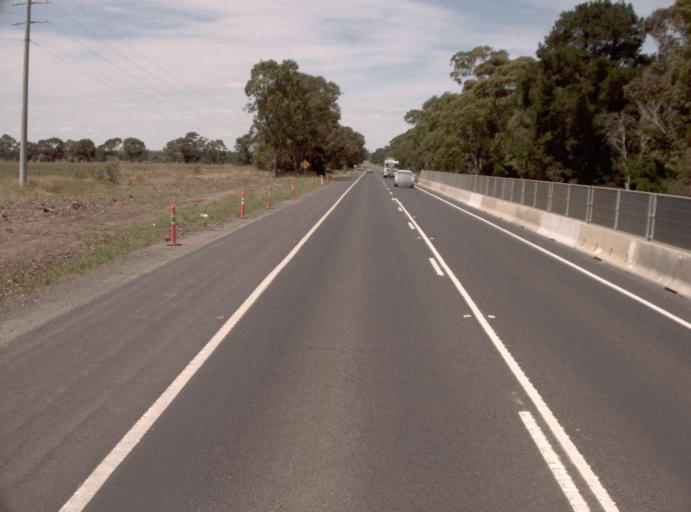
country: AU
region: Victoria
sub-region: Latrobe
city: Traralgon
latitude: -38.1850
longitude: 146.5948
